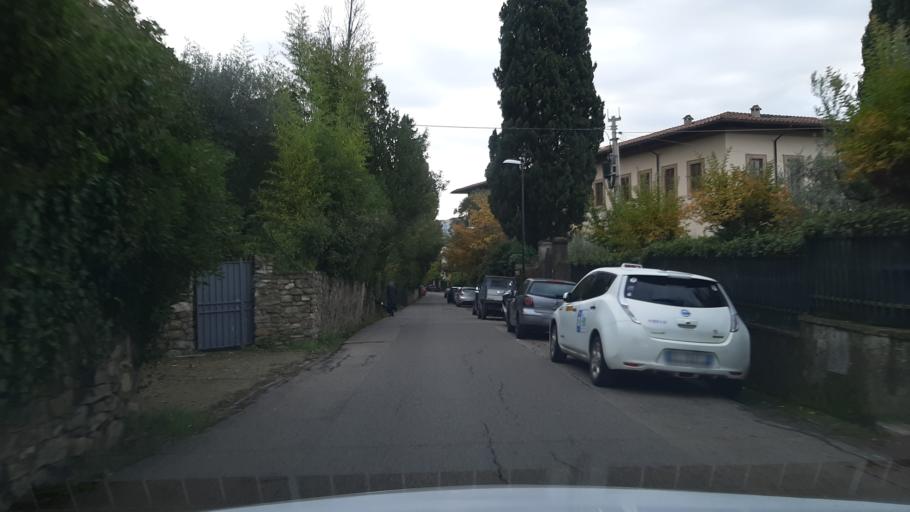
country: IT
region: Tuscany
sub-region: Province of Florence
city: Fiesole
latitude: 43.7820
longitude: 11.2983
